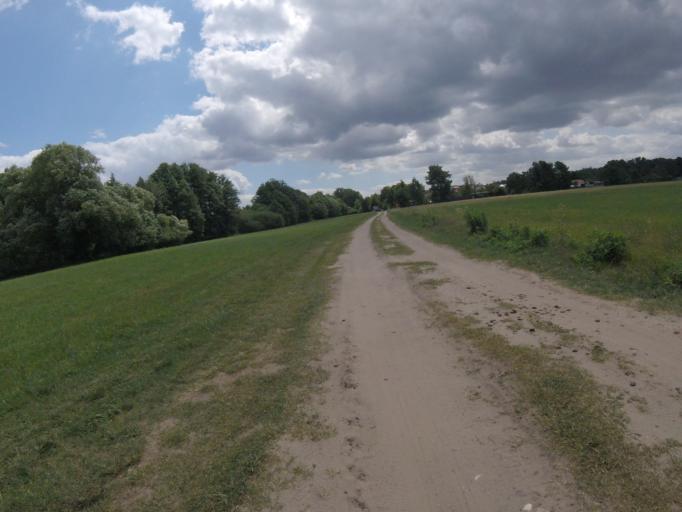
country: DE
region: Brandenburg
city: Bestensee
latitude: 52.2376
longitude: 13.6188
